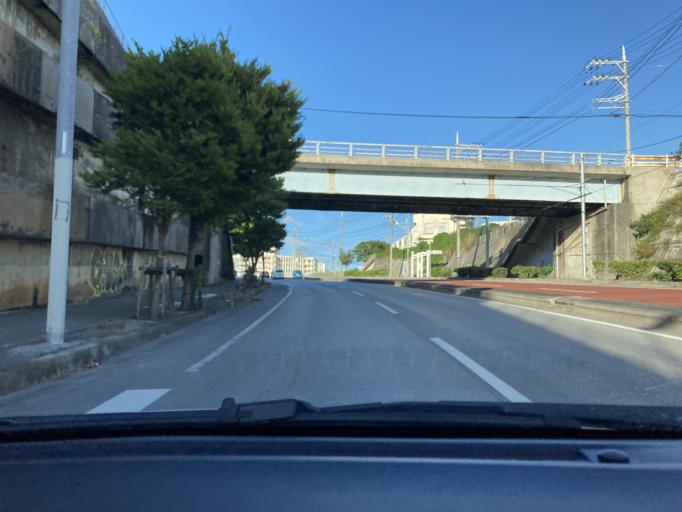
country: JP
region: Okinawa
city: Naha-shi
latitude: 26.2026
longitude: 127.7204
